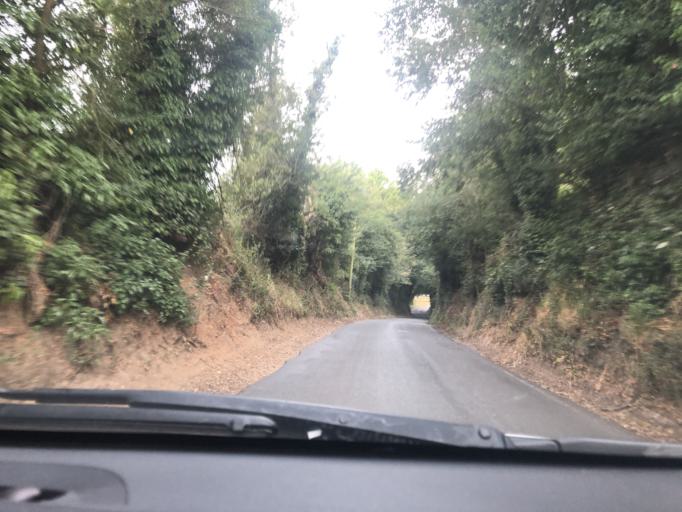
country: GB
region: England
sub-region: Kent
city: Herne Bay
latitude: 51.3501
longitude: 1.1644
